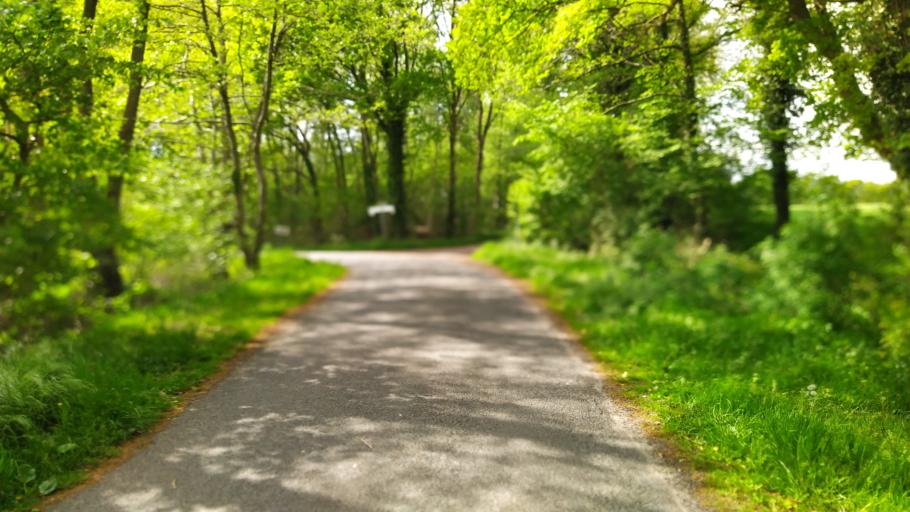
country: DE
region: Lower Saxony
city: Farven
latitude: 53.4267
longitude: 9.3442
